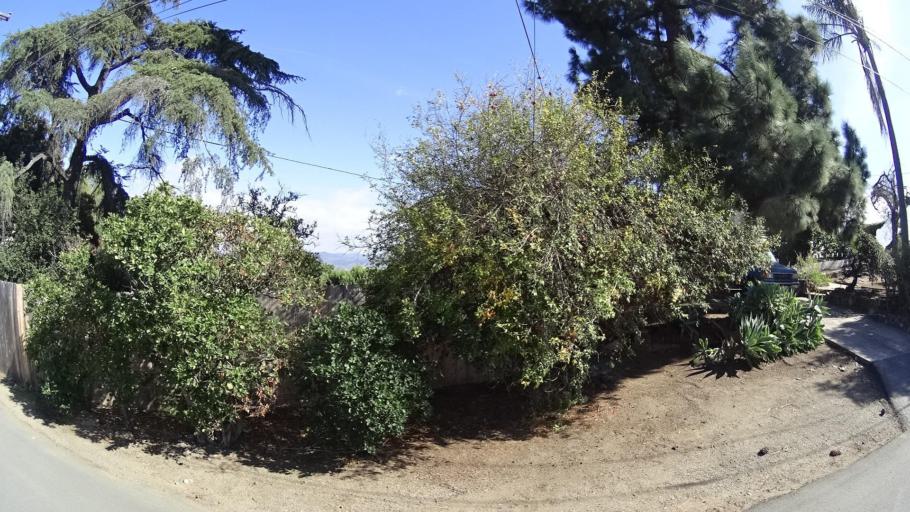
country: US
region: California
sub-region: San Diego County
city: Casa de Oro-Mount Helix
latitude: 32.7601
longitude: -116.9580
